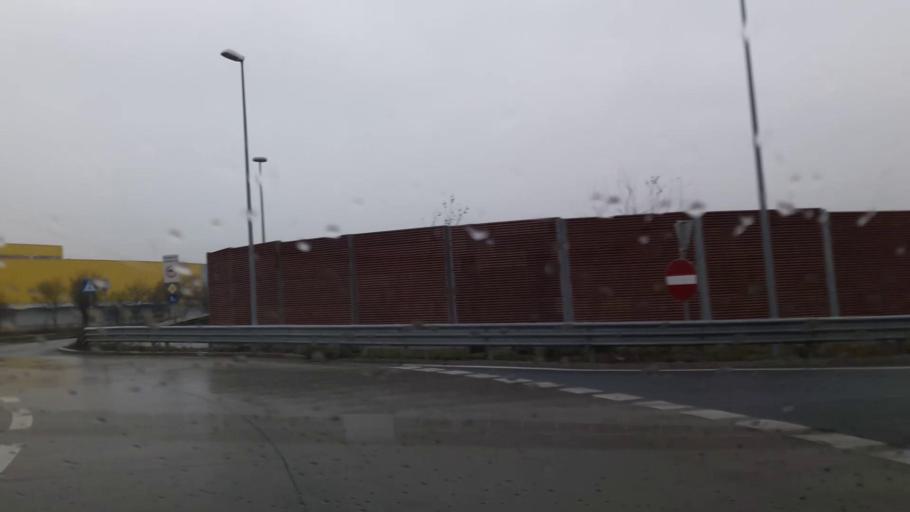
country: AT
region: Lower Austria
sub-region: Politischer Bezirk Wien-Umgebung
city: Gerasdorf bei Wien
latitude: 48.2682
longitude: 16.4772
